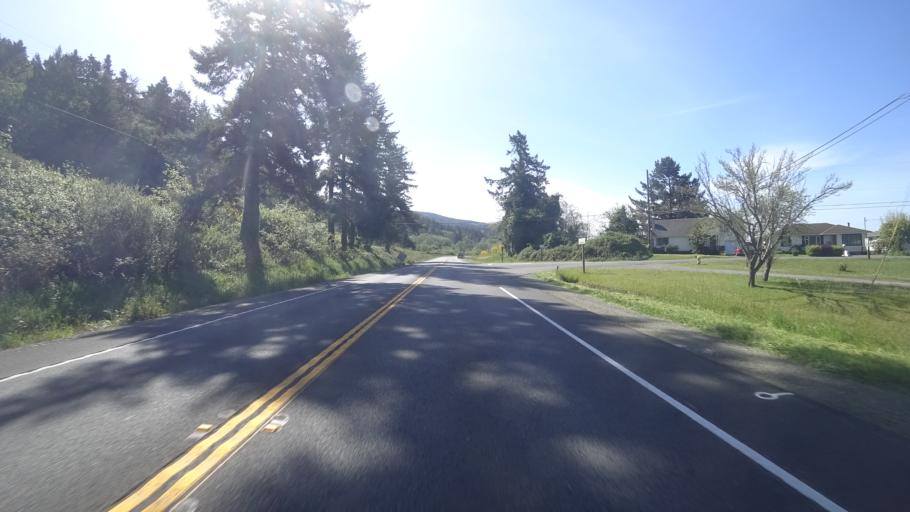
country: US
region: California
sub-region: Del Norte County
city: Bertsch-Oceanview
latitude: 41.9238
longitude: -124.1392
